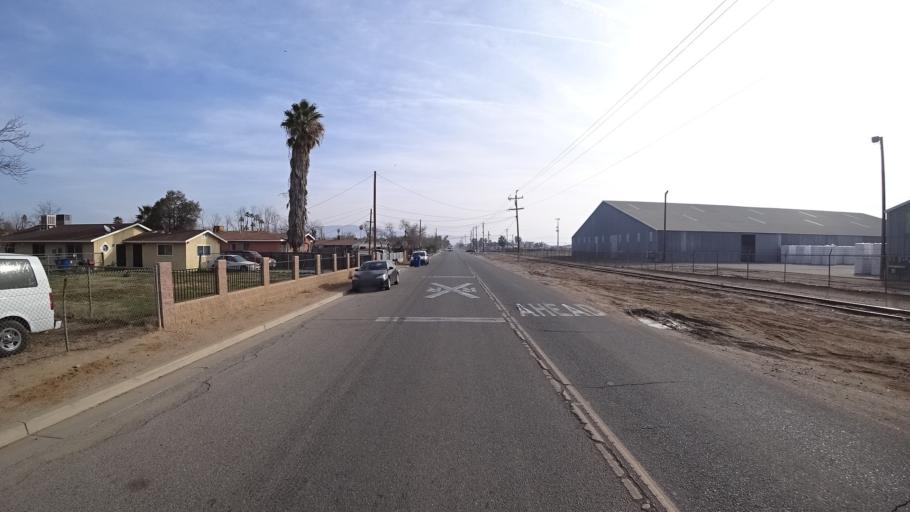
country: US
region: California
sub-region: Kern County
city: Bakersfield
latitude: 35.3613
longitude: -118.9782
